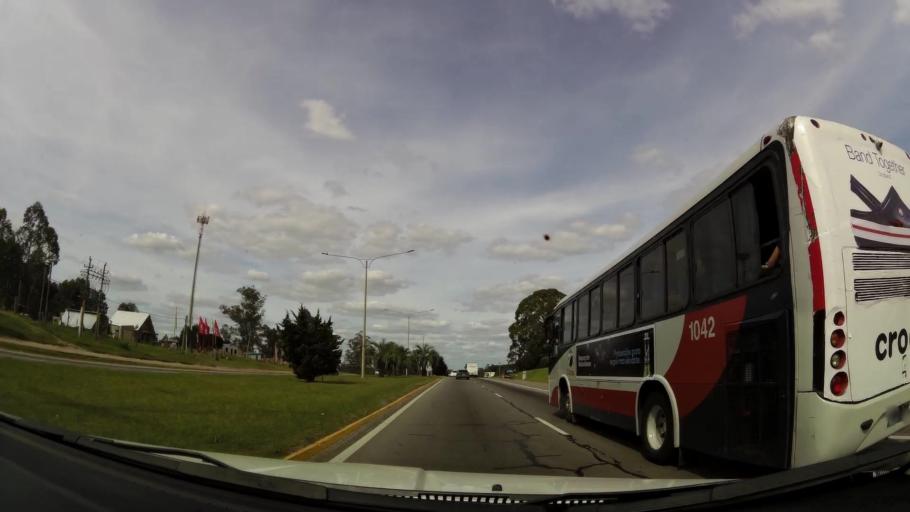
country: UY
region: Canelones
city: Empalme Olmos
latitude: -34.7822
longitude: -55.8801
